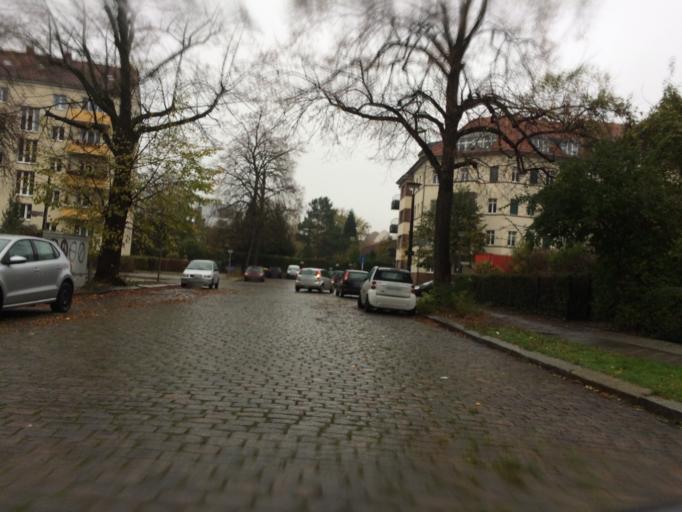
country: DE
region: Berlin
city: Pankow
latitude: 52.5631
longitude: 13.4186
